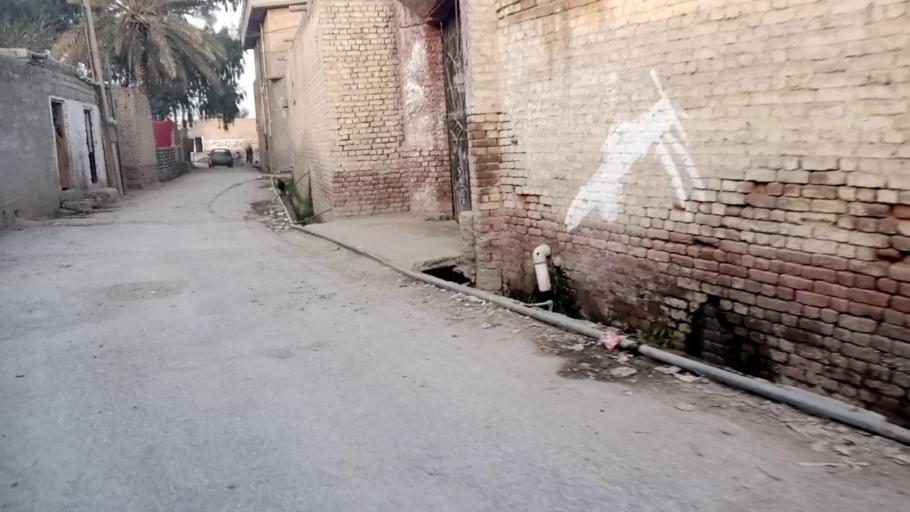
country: PK
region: Khyber Pakhtunkhwa
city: Peshawar
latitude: 34.0503
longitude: 71.4588
